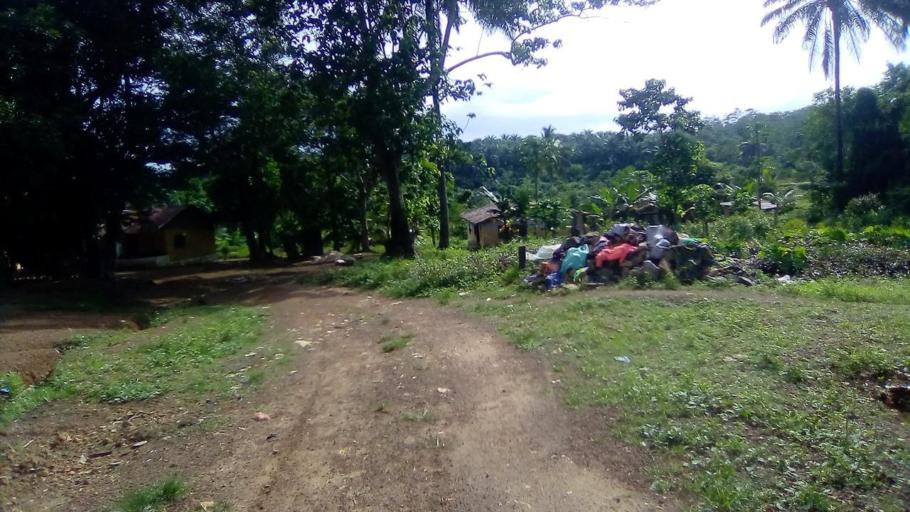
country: SL
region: Southern Province
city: Pujehun
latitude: 7.3603
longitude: -11.7218
